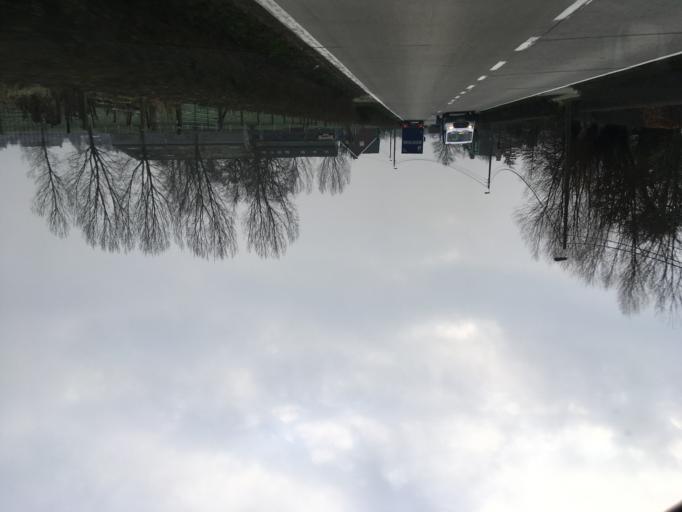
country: BE
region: Flanders
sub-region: Provincie West-Vlaanderen
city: Oostrozebeke
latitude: 50.9388
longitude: 3.3407
